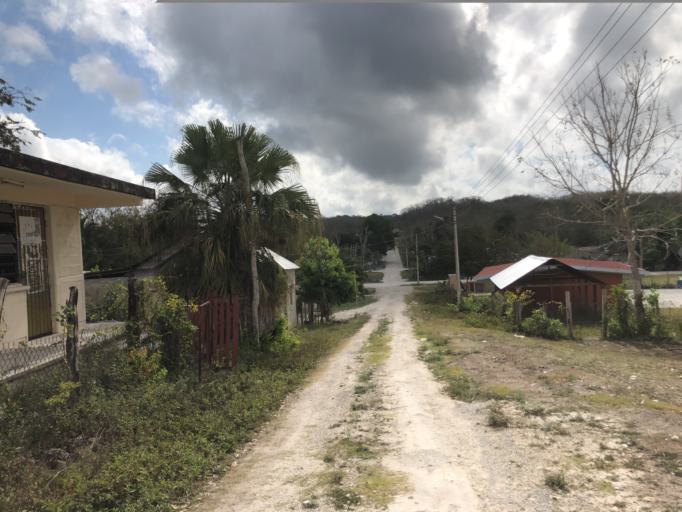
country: MX
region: Quintana Roo
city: Nicolas Bravo
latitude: 18.4524
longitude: -89.3075
